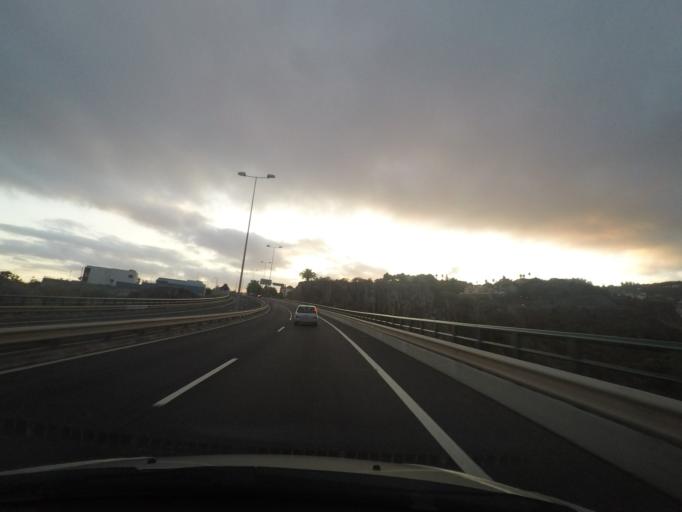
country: PT
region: Madeira
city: Canico
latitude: 32.6497
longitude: -16.8317
